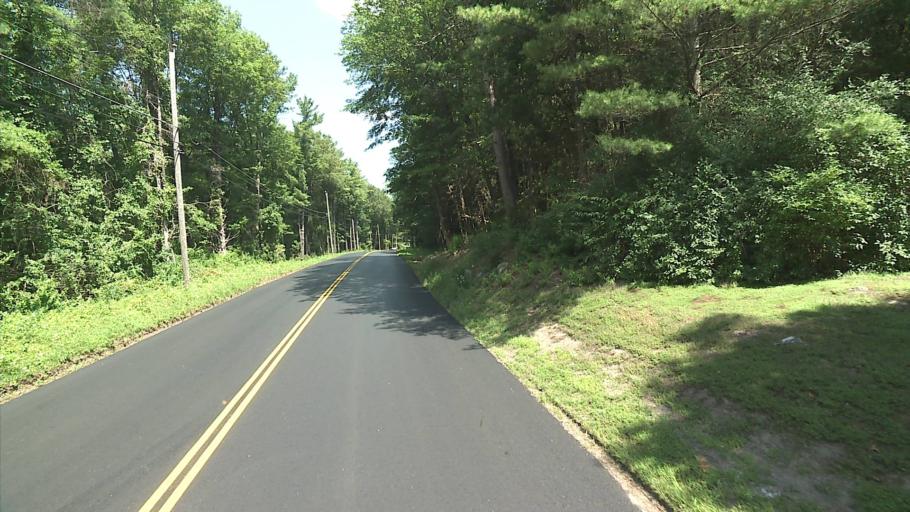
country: US
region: Connecticut
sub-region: Litchfield County
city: Canaan
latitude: 41.9973
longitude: -73.3603
